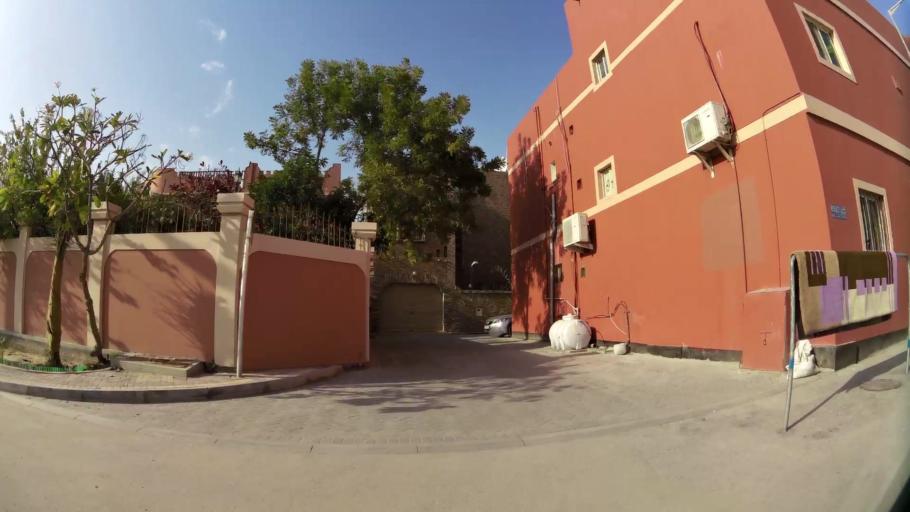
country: BH
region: Manama
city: Jidd Hafs
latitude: 26.2122
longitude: 50.5127
